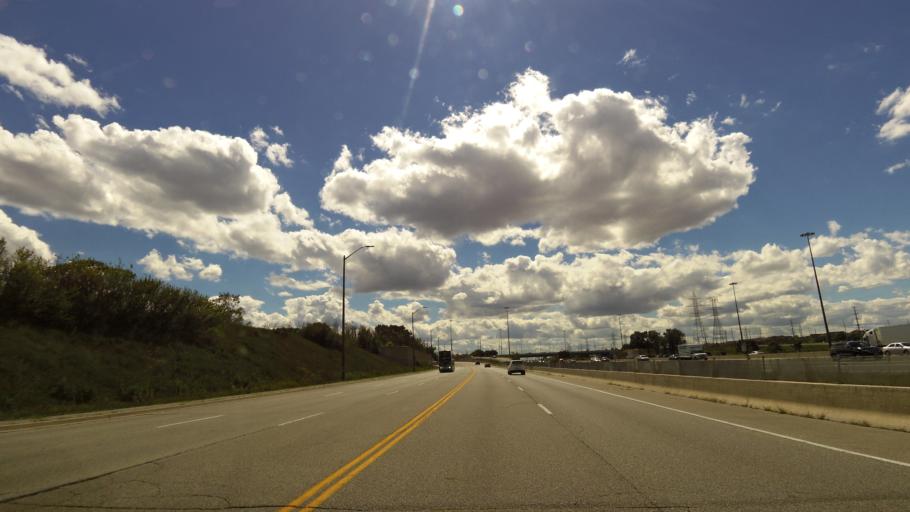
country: CA
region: Ontario
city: Mississauga
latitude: 43.5883
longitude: -79.6570
